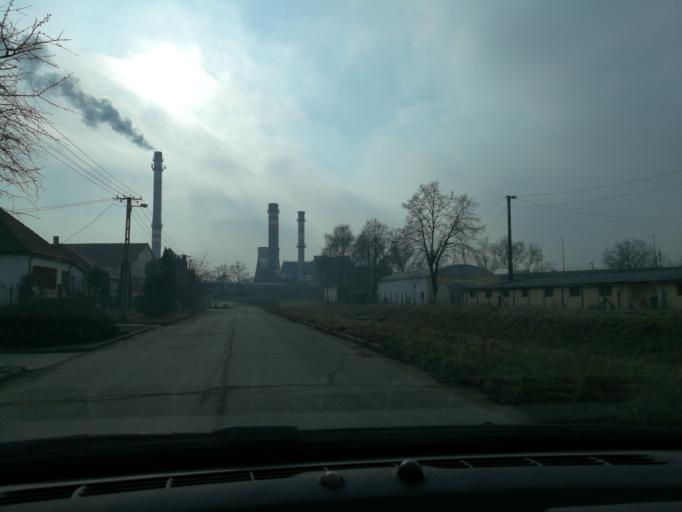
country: HU
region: Szabolcs-Szatmar-Bereg
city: Nyiregyhaza
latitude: 47.9593
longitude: 21.6990
